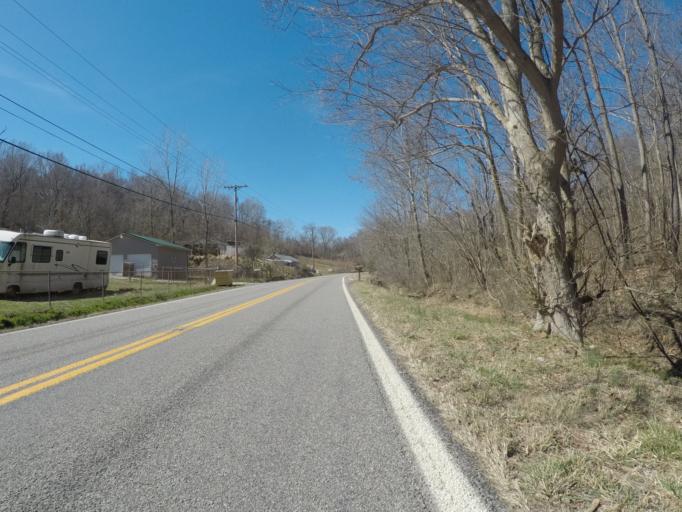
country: US
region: Ohio
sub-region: Lawrence County
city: Burlington
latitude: 38.4932
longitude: -82.5336
